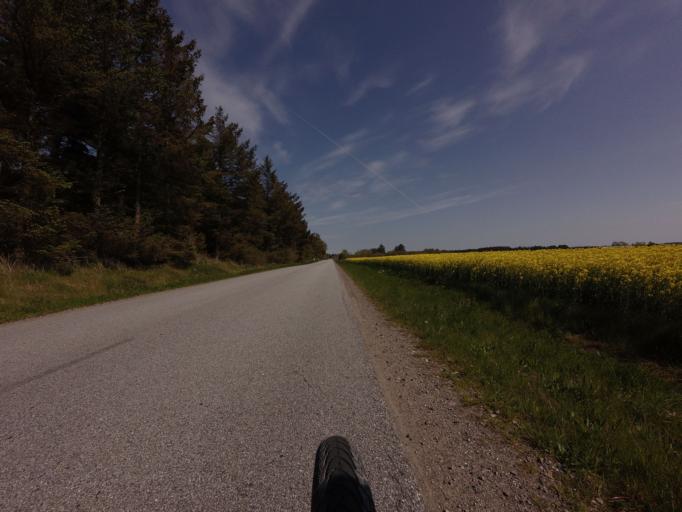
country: DK
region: North Denmark
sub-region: Jammerbugt Kommune
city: Pandrup
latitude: 57.2288
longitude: 9.6159
